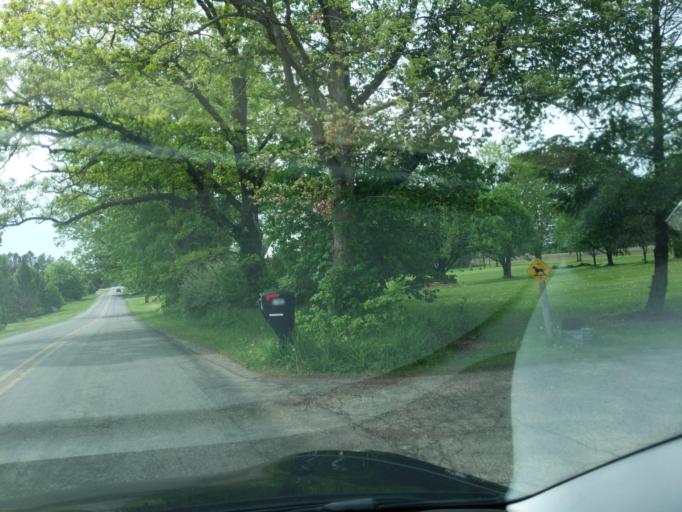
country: US
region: Michigan
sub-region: Ingham County
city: Leslie
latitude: 42.4247
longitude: -84.3079
